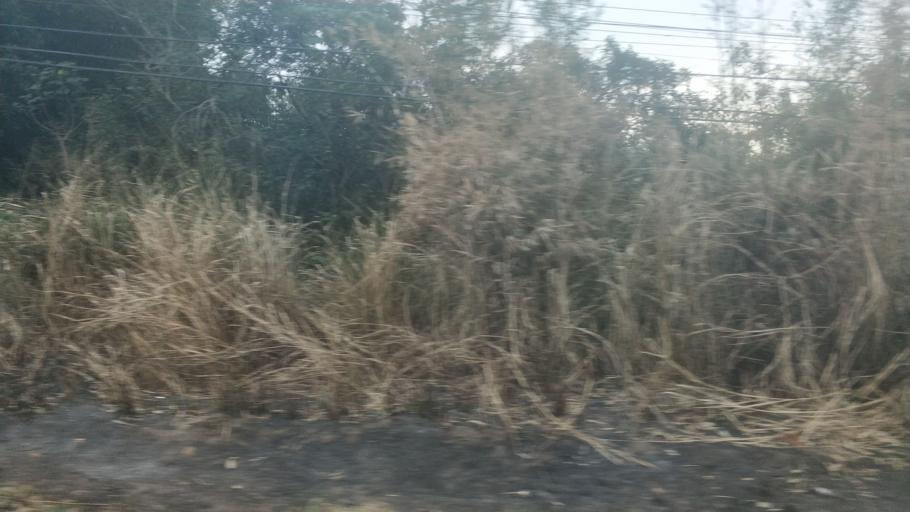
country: BR
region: Rio de Janeiro
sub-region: Seropedica
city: Seropedica
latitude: -22.7703
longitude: -43.6731
